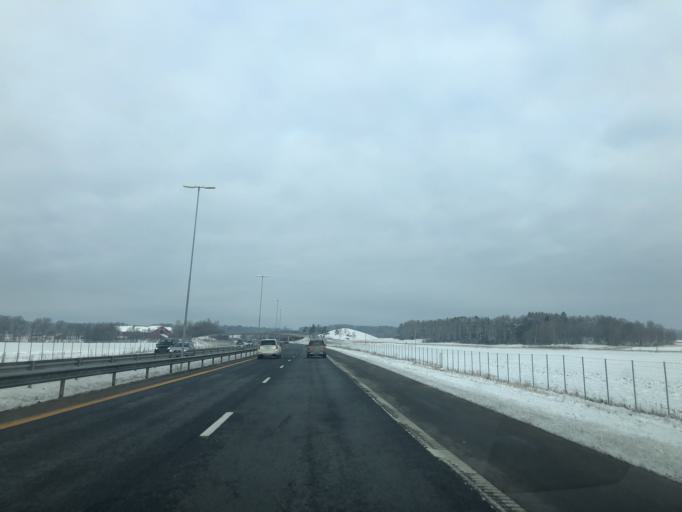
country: NO
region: Ostfold
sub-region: Sarpsborg
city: Skjeberg
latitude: 59.1415
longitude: 11.2553
